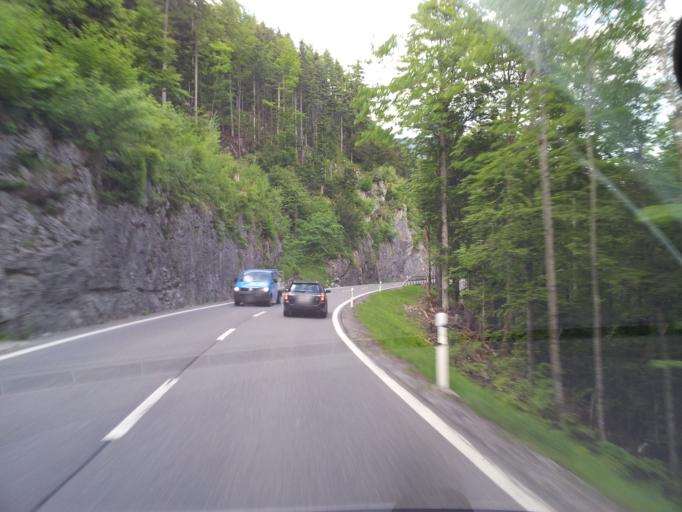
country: CH
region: Obwalden
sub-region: Obwalden
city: Lungern
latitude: 46.7676
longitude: 8.1448
